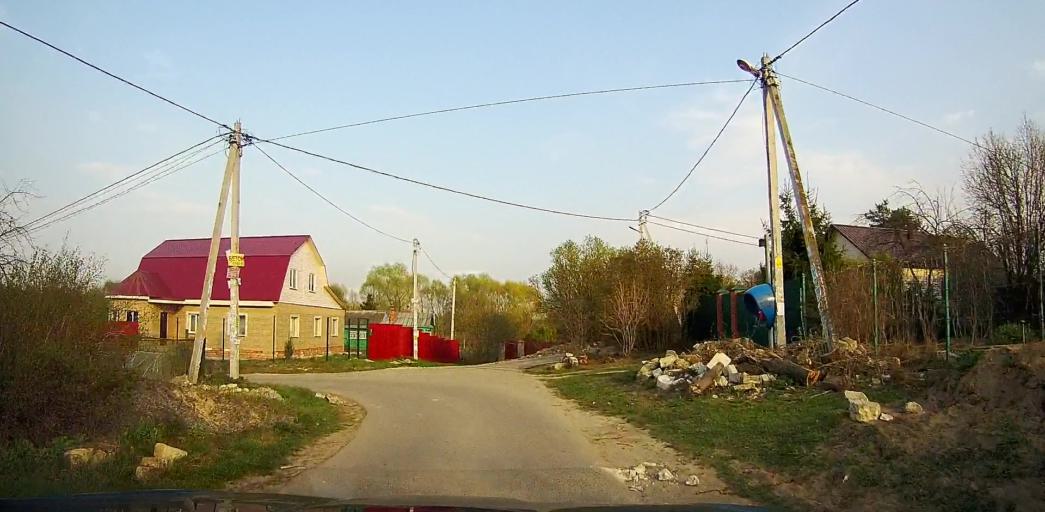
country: RU
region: Moskovskaya
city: Andreyevskoye
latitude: 55.5472
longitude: 37.9622
